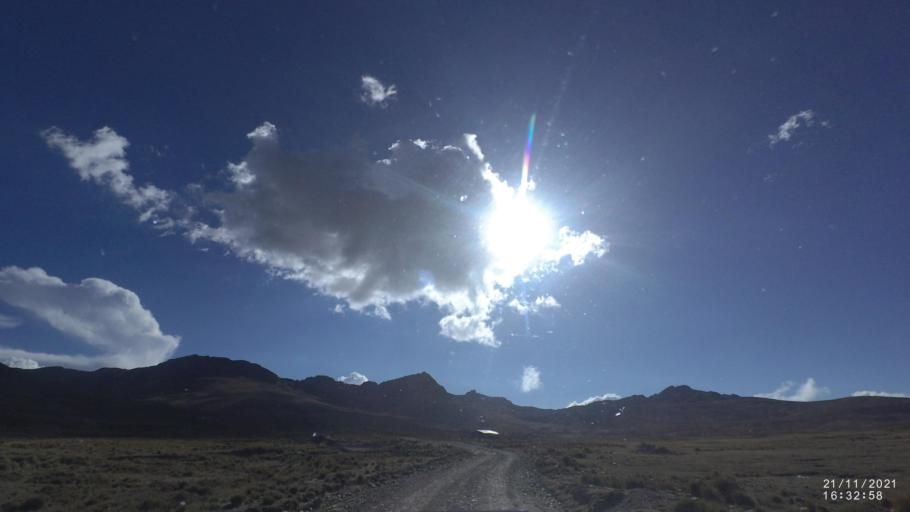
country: BO
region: Cochabamba
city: Cochabamba
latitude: -17.0317
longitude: -66.2774
